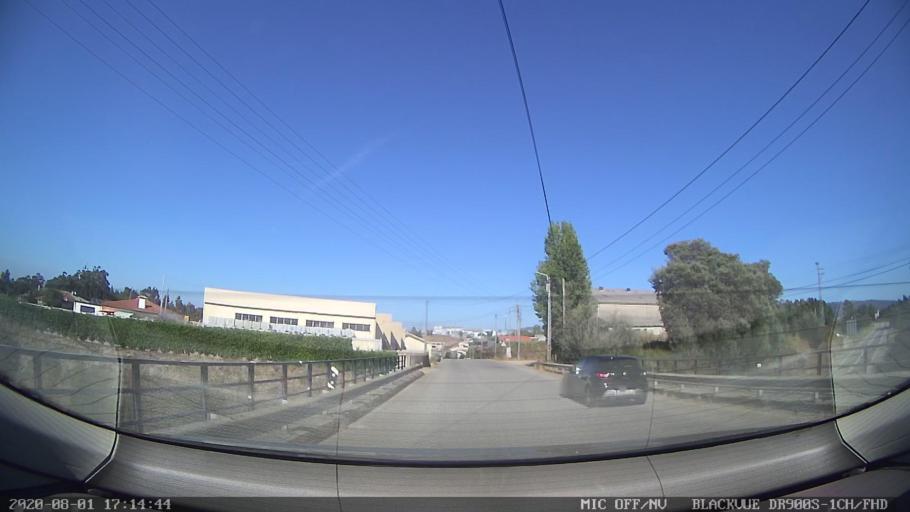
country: PT
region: Porto
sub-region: Santo Tirso
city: Santo Tirso
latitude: 41.3370
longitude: -8.5006
